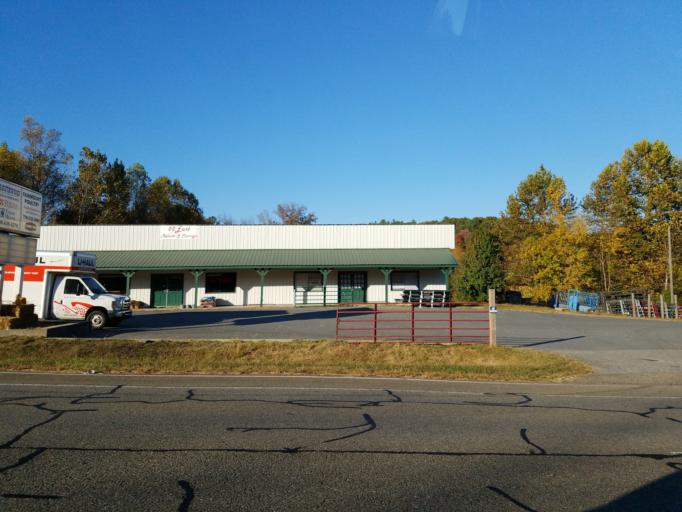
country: US
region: Georgia
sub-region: Gilmer County
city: Ellijay
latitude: 34.6511
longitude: -84.4041
